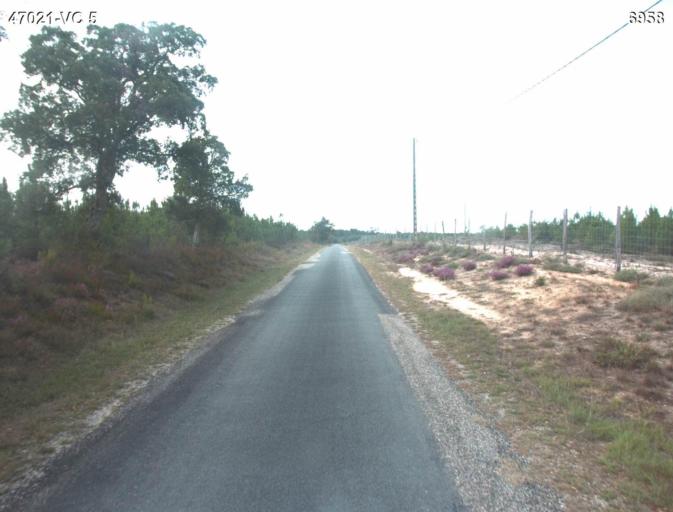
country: FR
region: Aquitaine
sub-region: Departement du Lot-et-Garonne
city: Barbaste
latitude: 44.1515
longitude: 0.2148
